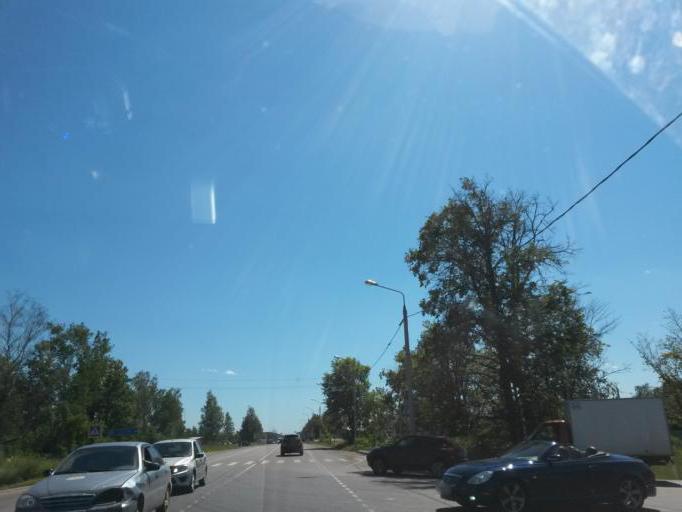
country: RU
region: Moskovskaya
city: Proletarskiy
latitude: 55.0314
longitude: 37.4282
